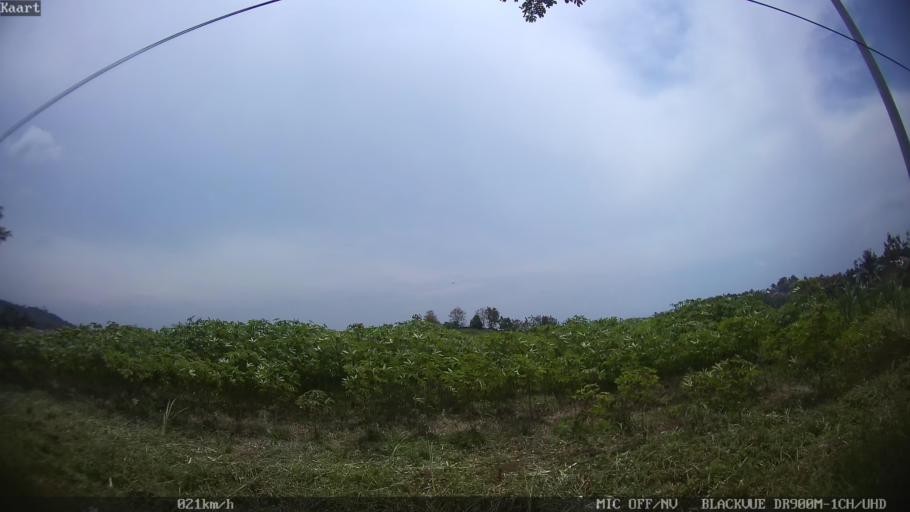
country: ID
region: Lampung
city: Bandarlampung
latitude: -5.4114
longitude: 105.2044
